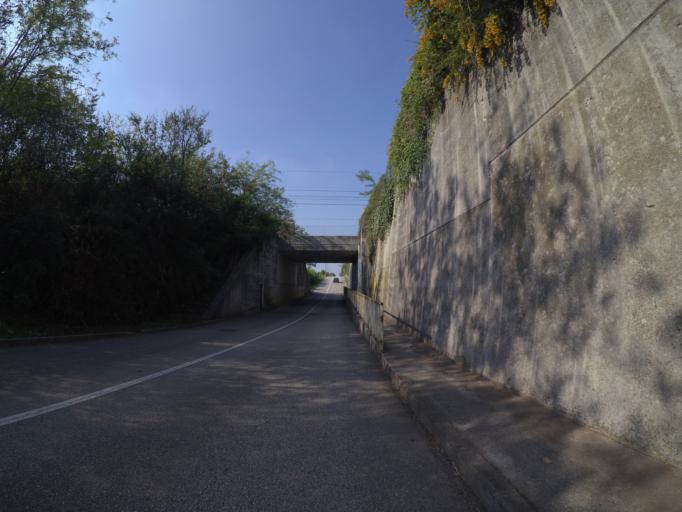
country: IT
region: Friuli Venezia Giulia
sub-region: Provincia di Udine
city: Basiliano
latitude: 45.9855
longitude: 13.0333
